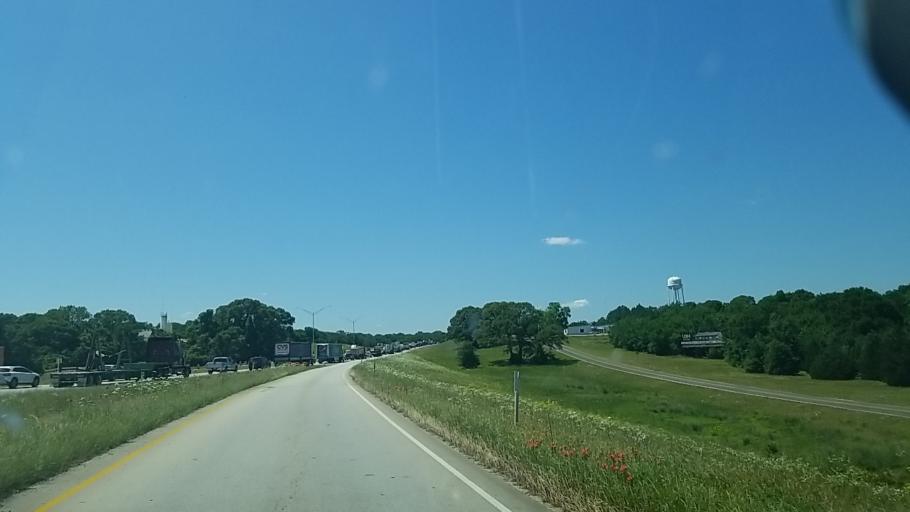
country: US
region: Texas
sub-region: Leon County
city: Buffalo
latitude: 31.4535
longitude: -96.0778
